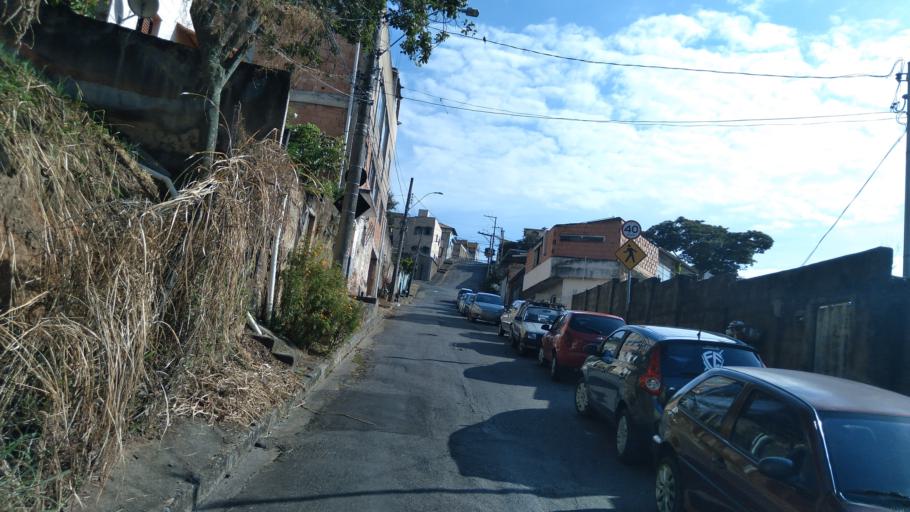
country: BR
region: Minas Gerais
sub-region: Belo Horizonte
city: Belo Horizonte
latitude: -19.8971
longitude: -43.9420
